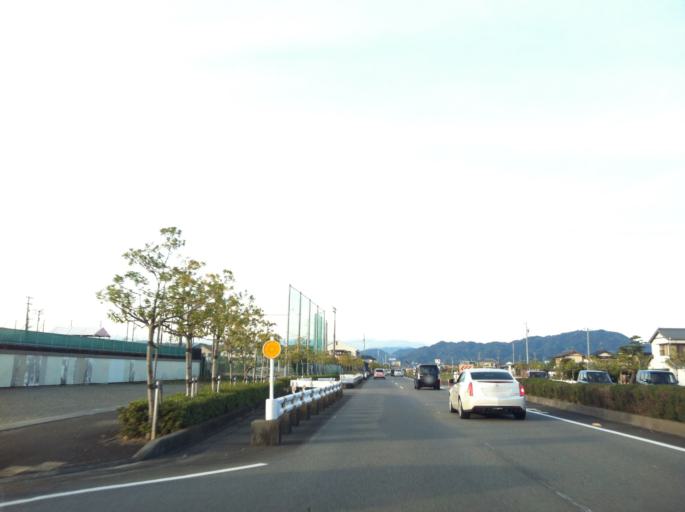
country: JP
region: Shizuoka
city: Yaizu
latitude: 34.8385
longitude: 138.3002
